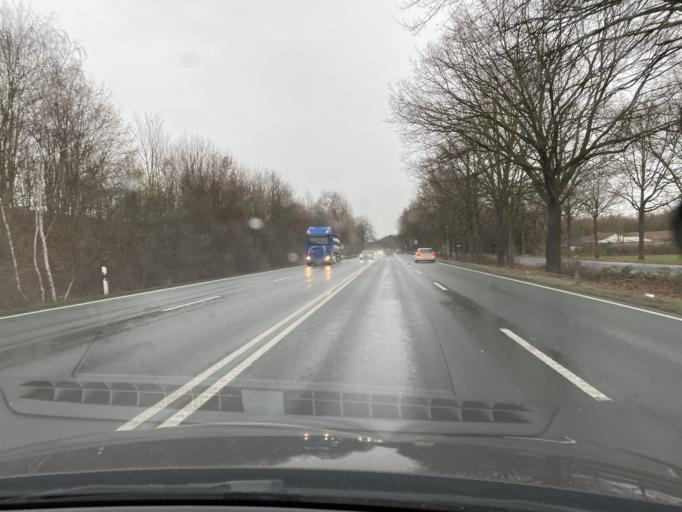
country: DE
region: North Rhine-Westphalia
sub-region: Regierungsbezirk Arnsberg
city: Lippstadt
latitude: 51.6914
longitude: 8.3631
